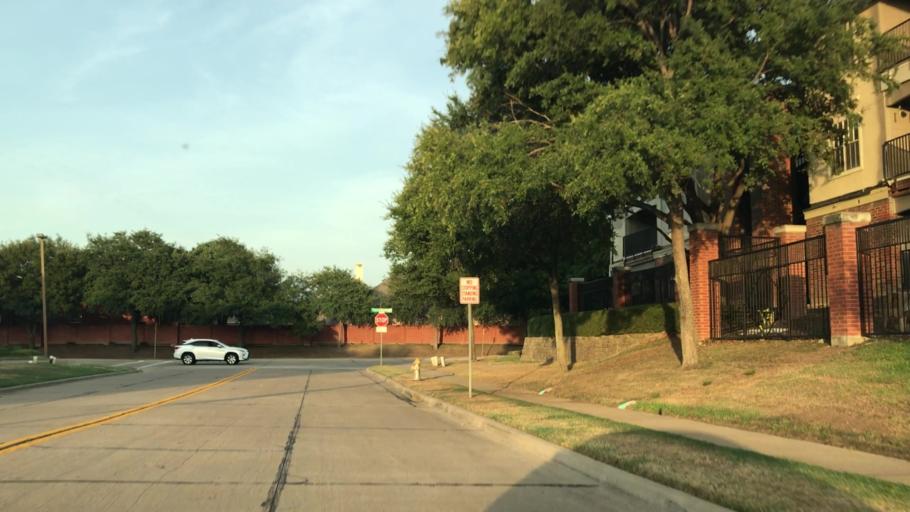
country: US
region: Texas
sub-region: Dallas County
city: Farmers Branch
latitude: 32.9300
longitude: -96.9464
